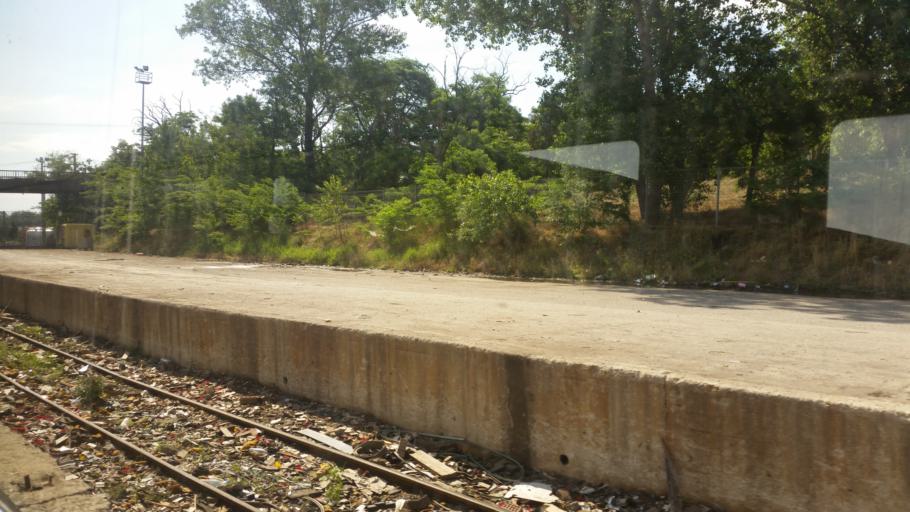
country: TR
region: Tekirdag
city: Corlu
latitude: 41.1780
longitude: 27.7746
